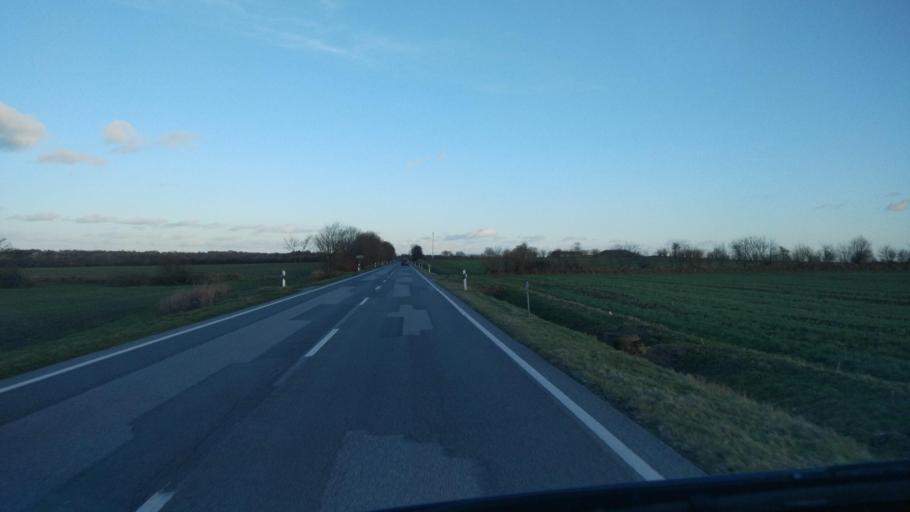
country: DE
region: Schleswig-Holstein
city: Wittbek
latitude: 54.4617
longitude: 9.1902
